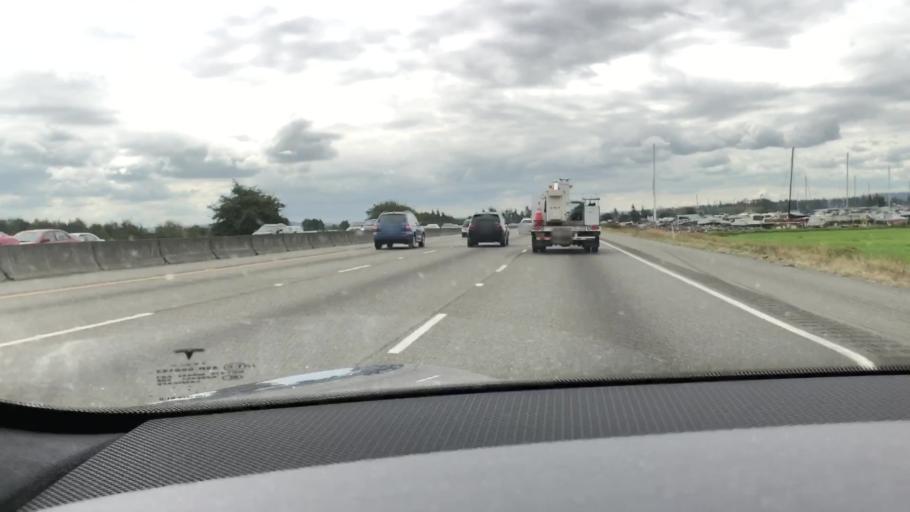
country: US
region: Washington
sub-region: Snohomish County
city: Marysville
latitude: 48.0175
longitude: -122.1751
